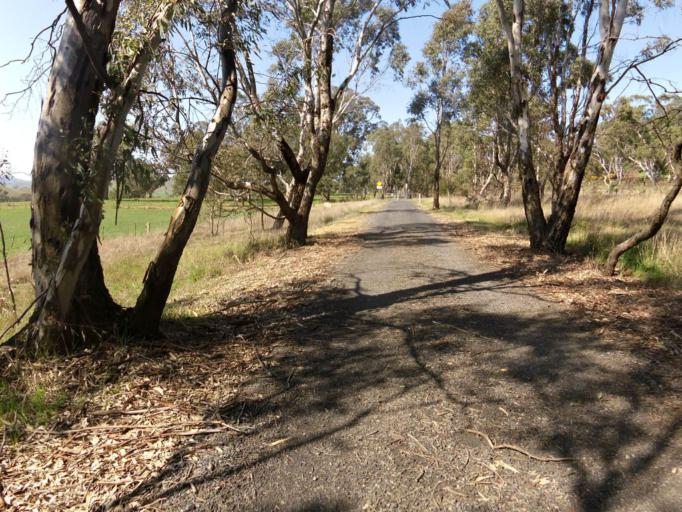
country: AU
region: Victoria
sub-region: Murrindindi
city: Alexandra
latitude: -37.0144
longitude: 145.7790
